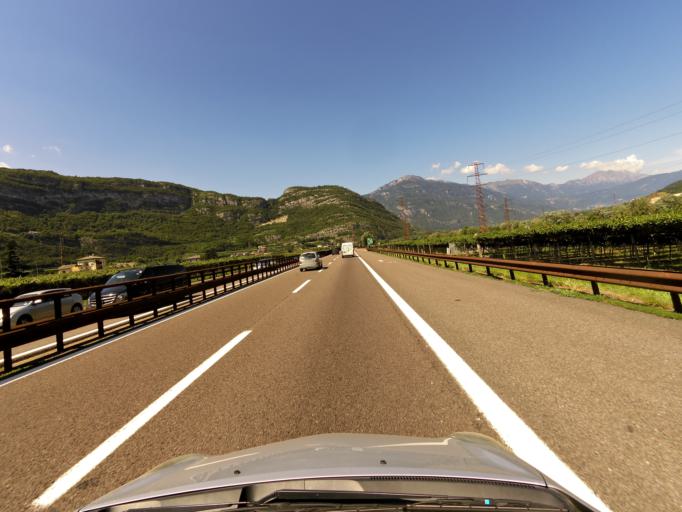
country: IT
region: Trentino-Alto Adige
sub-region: Provincia di Trento
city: Marco
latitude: 45.8163
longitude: 11.0080
